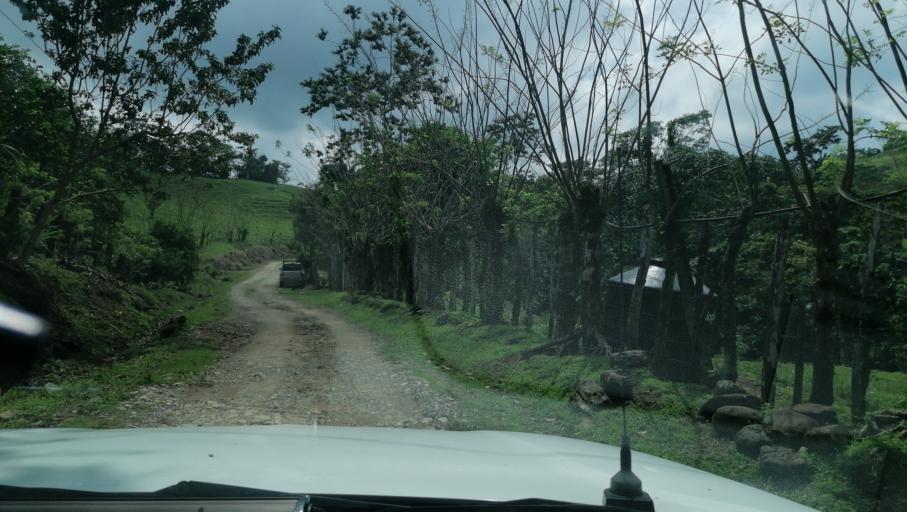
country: MX
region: Chiapas
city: Pichucalco
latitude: 17.4524
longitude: -93.1984
